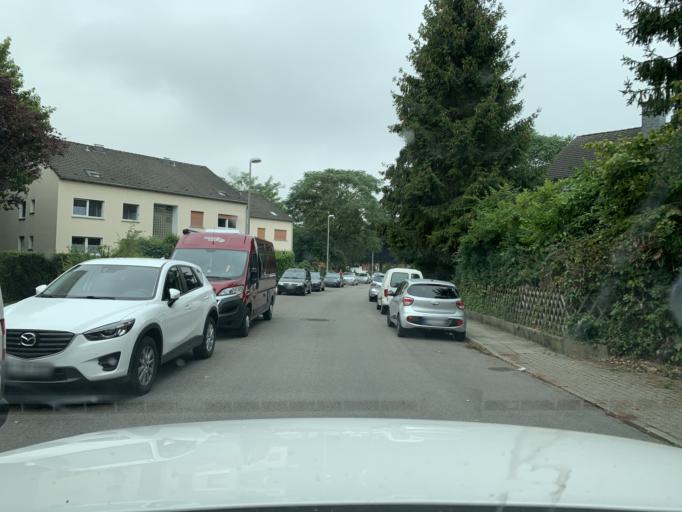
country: DE
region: North Rhine-Westphalia
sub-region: Regierungsbezirk Dusseldorf
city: Muelheim (Ruhr)
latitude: 51.3943
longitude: 6.8707
